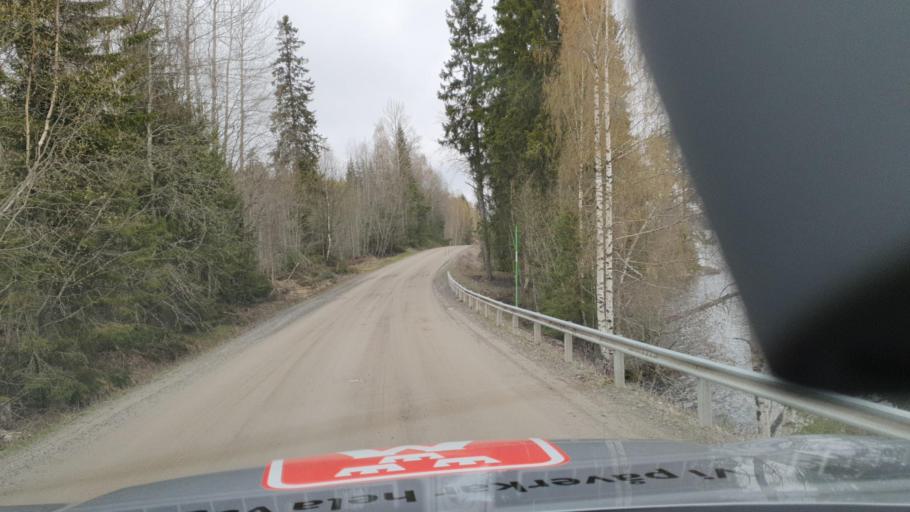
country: SE
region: Vaesternorrland
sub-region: OErnskoeldsviks Kommun
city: Husum
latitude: 63.6347
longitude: 19.0590
